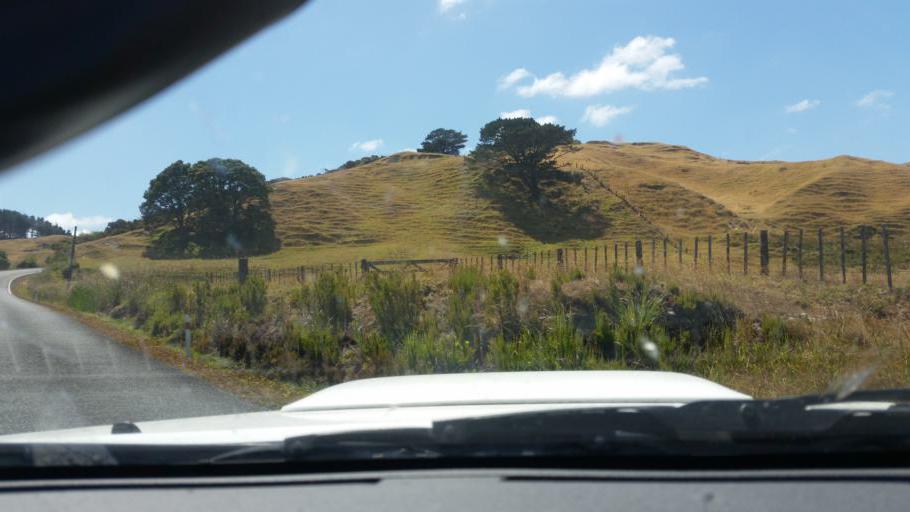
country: NZ
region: Northland
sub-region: Kaipara District
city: Dargaville
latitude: -35.8225
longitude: 173.6816
